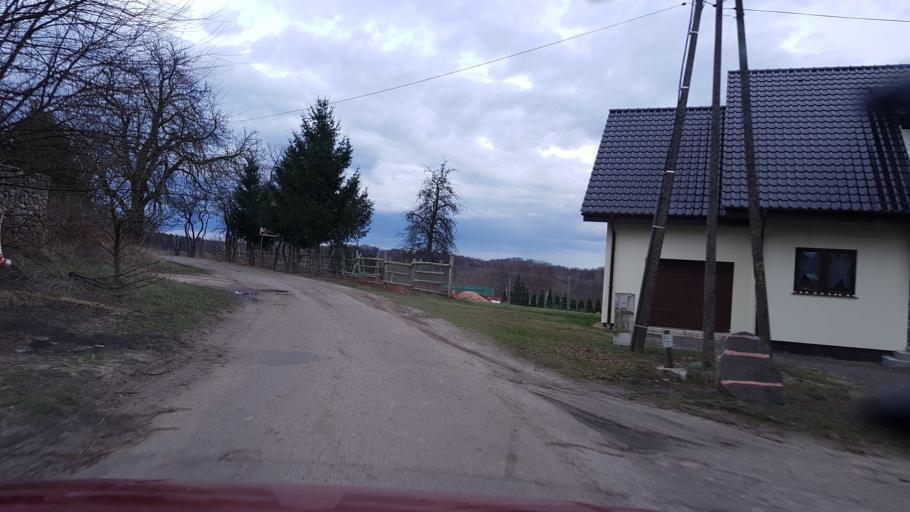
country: PL
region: West Pomeranian Voivodeship
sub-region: Powiat gryfinski
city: Stare Czarnowo
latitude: 53.3247
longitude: 14.6832
